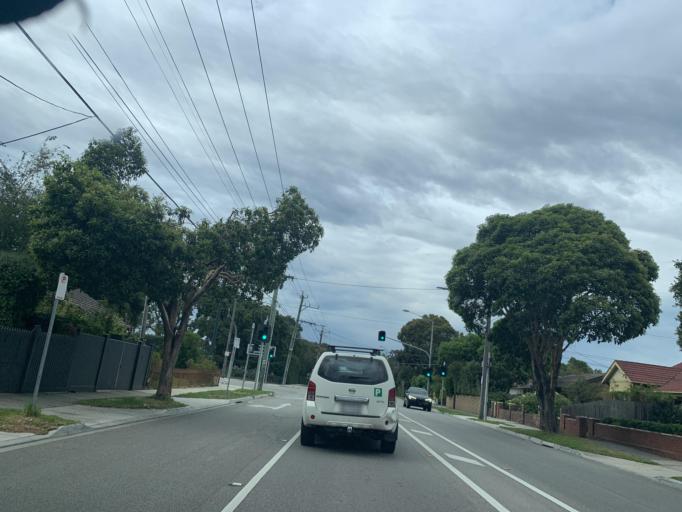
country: AU
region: Victoria
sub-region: Stonnington
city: Malvern East
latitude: -37.8764
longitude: 145.0356
